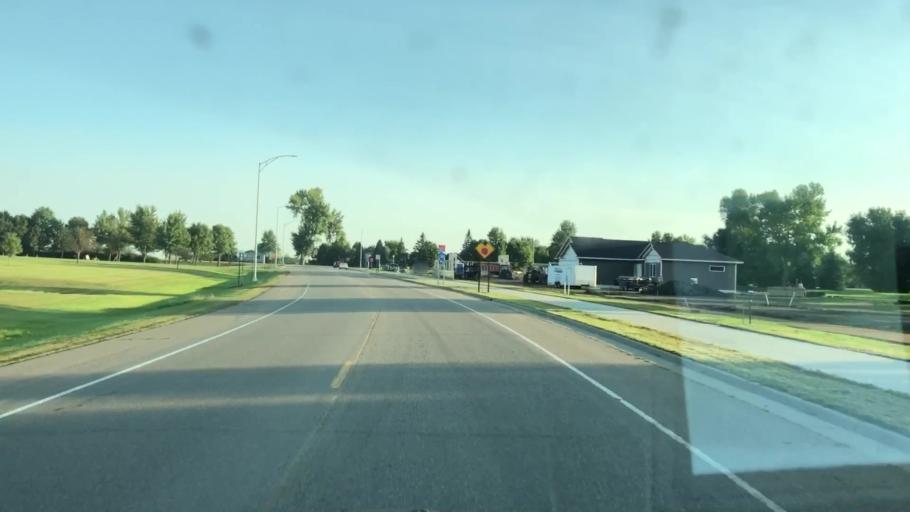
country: US
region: Minnesota
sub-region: Nobles County
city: Worthington
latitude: 43.6284
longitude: -95.6287
